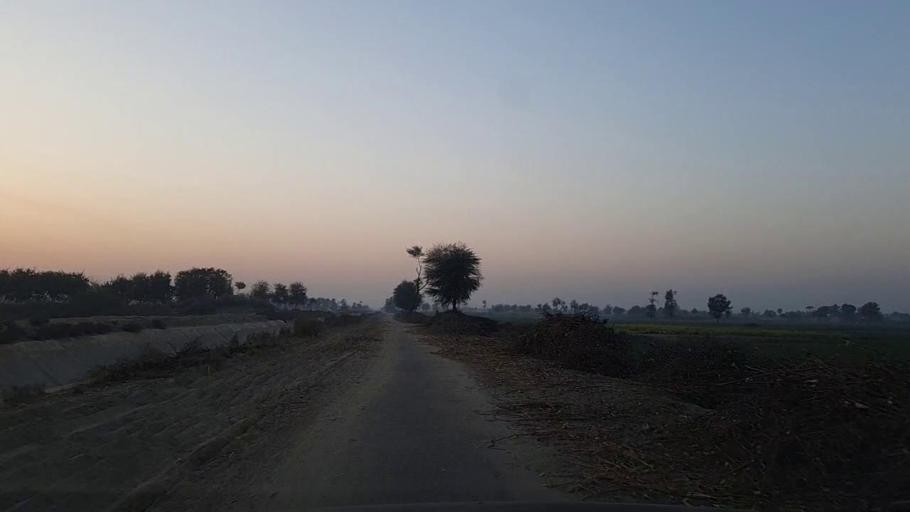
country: PK
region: Sindh
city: Daur
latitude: 26.4772
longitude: 68.4971
